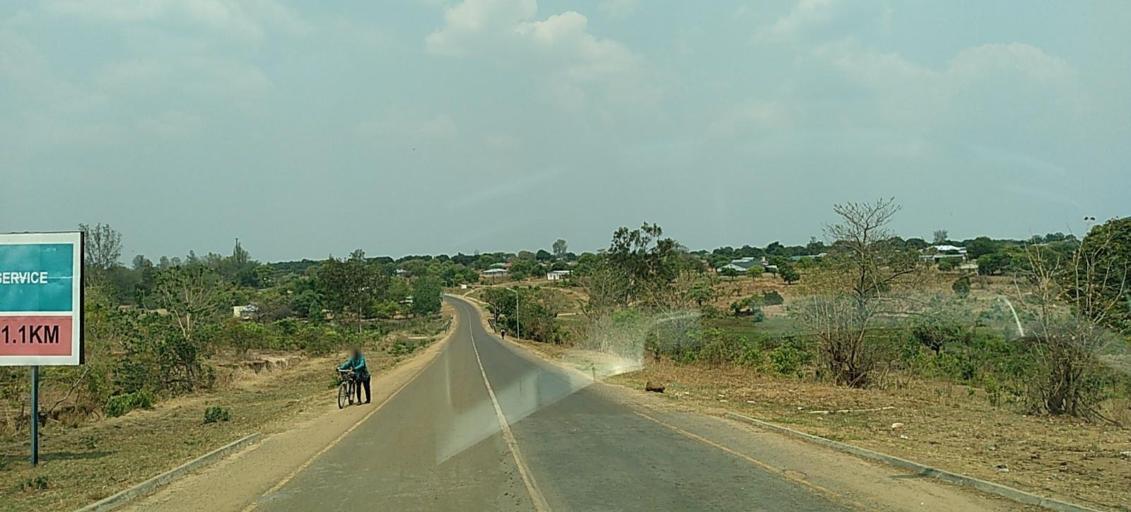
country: ZM
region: North-Western
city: Zambezi
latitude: -13.5494
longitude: 23.1063
